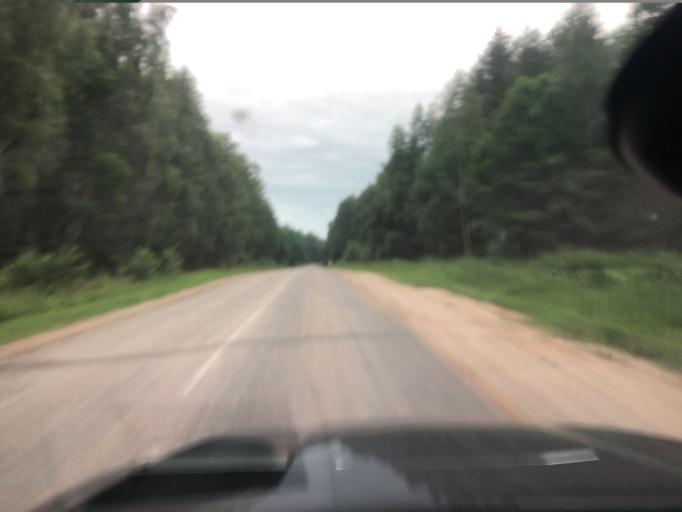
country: RU
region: Jaroslavl
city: Petrovsk
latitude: 56.9874
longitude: 39.1937
